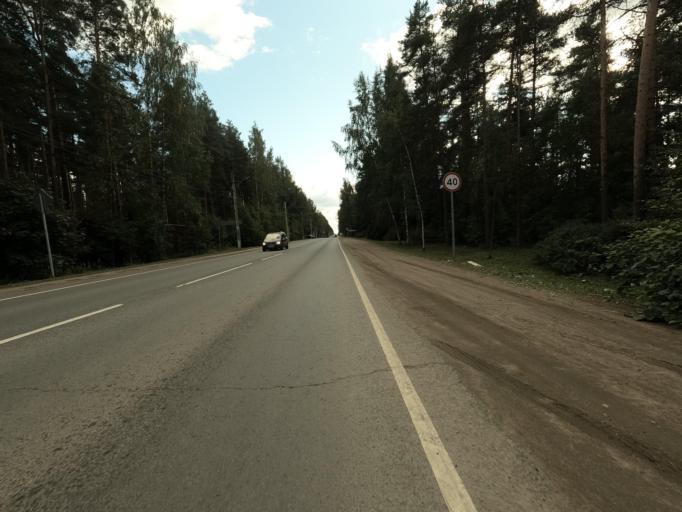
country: RU
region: Leningrad
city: Vsevolozhsk
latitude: 60.0049
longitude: 30.6636
